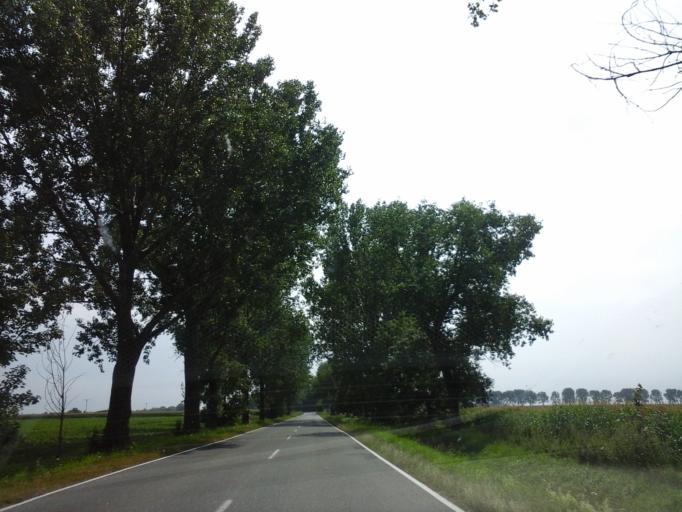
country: PL
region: Lower Silesian Voivodeship
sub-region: Powiat wroclawski
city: Zorawina
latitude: 50.8839
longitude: 17.0618
